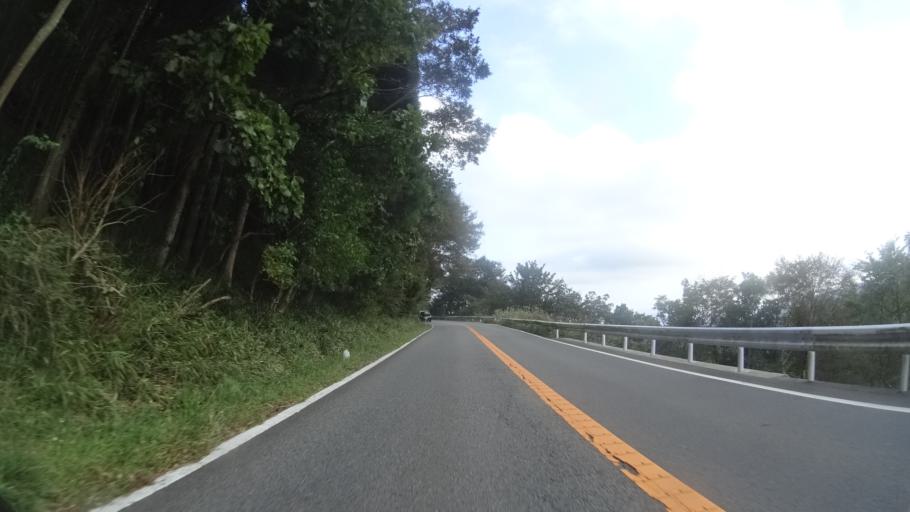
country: JP
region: Oita
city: Beppu
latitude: 33.2692
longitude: 131.4173
